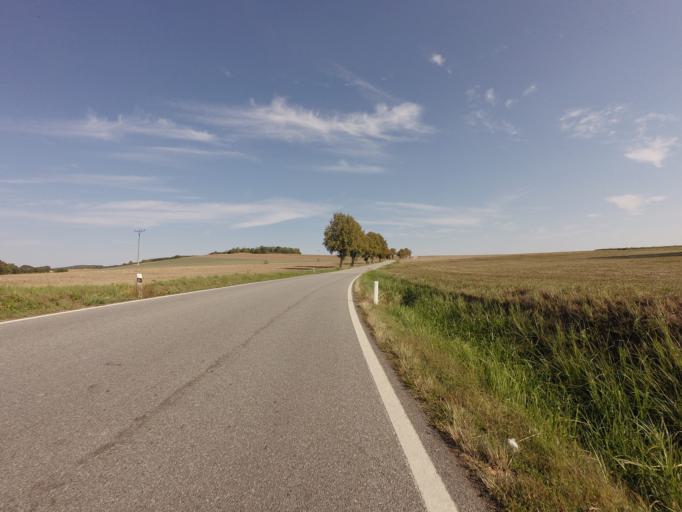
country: CZ
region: Jihocesky
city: Tyn nad Vltavou
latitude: 49.2815
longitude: 14.3962
